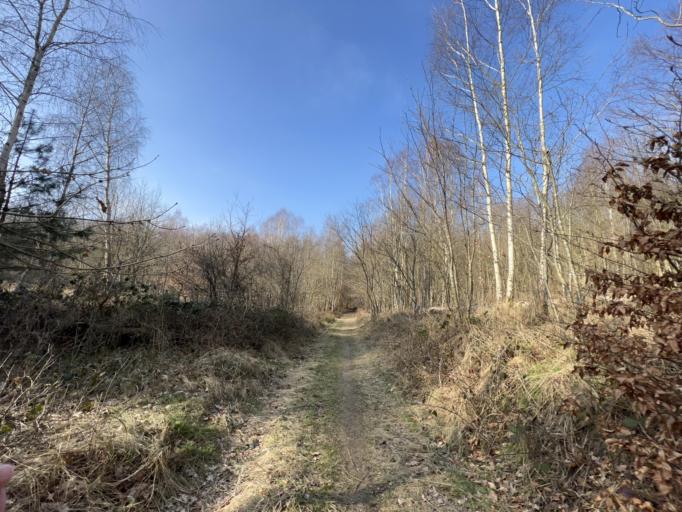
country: DE
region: Mecklenburg-Vorpommern
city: Sagard
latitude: 54.4799
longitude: 13.5557
